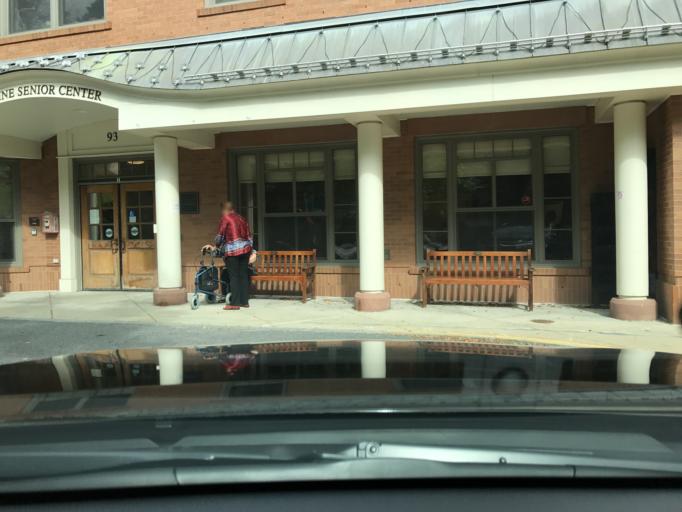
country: US
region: Massachusetts
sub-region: Norfolk County
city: Brookline
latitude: 42.3434
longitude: -71.1279
